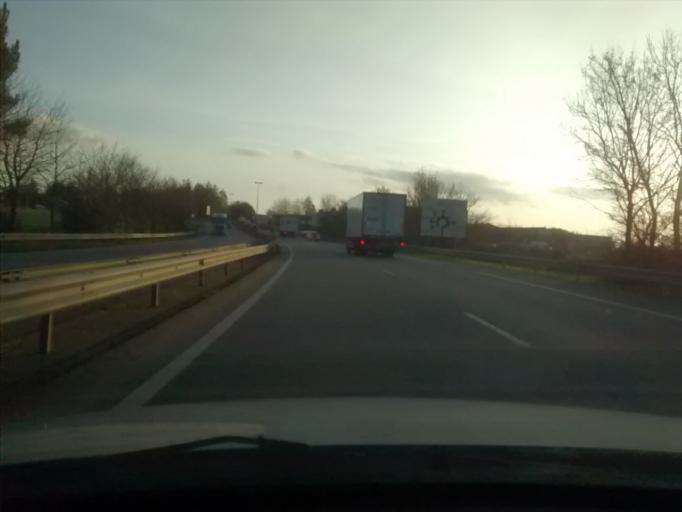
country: FR
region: Pays de la Loire
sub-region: Departement de la Mayenne
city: Bonchamp-les-Laval
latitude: 48.0754
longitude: -0.7305
